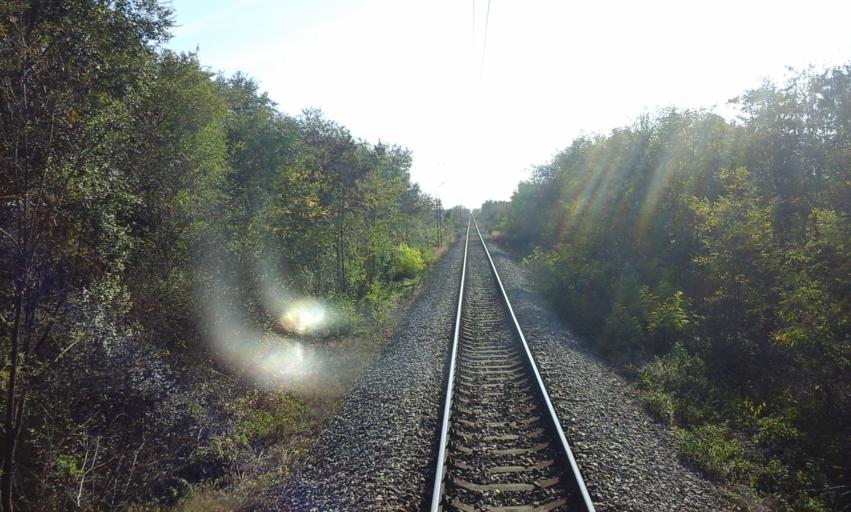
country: RS
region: Autonomna Pokrajina Vojvodina
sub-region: Severnobacki Okrug
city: Backa Topola
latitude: 45.8439
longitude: 19.6535
